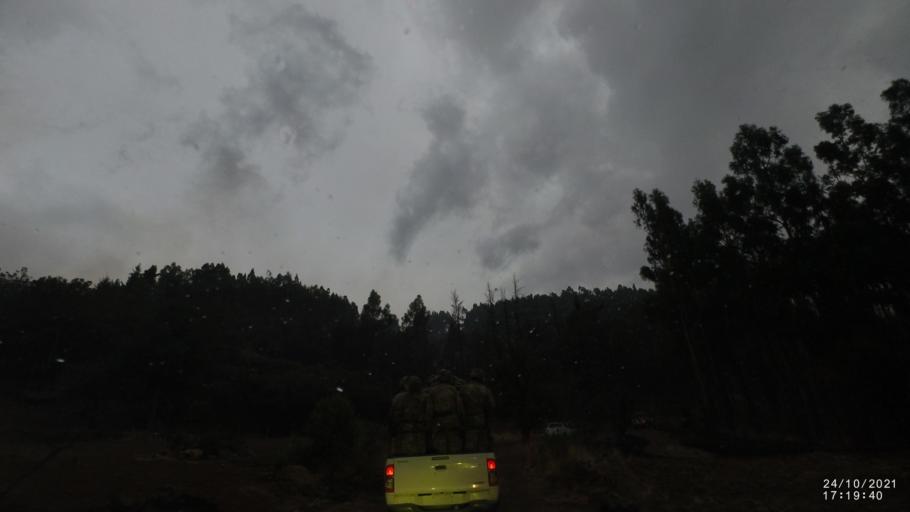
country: BO
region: Cochabamba
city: Cochabamba
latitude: -17.3282
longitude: -66.1370
